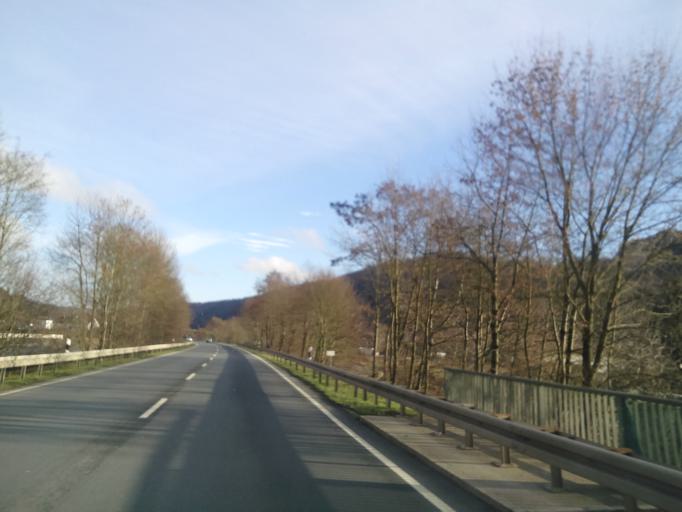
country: DE
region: Bavaria
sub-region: Upper Franconia
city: Kulmbach
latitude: 50.1131
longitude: 11.4587
